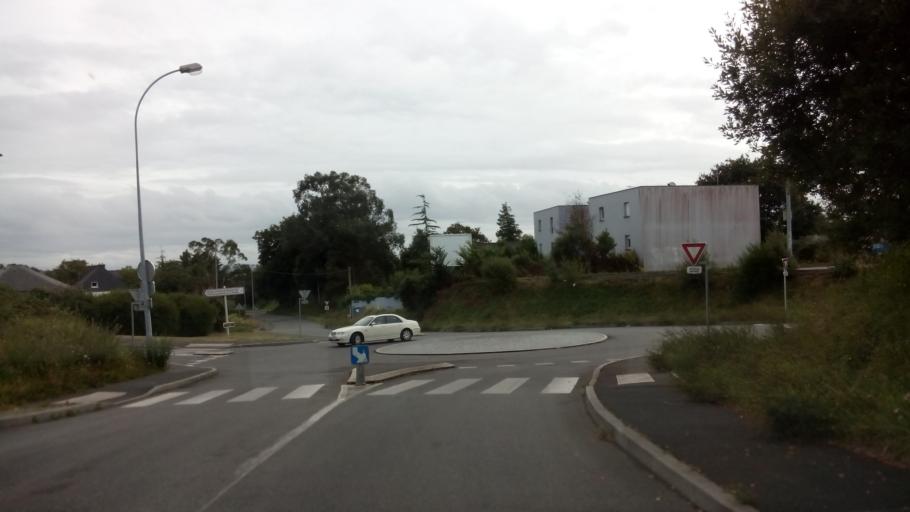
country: FR
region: Brittany
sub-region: Departement des Cotes-d'Armor
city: Lannion
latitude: 48.7488
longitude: -3.4576
